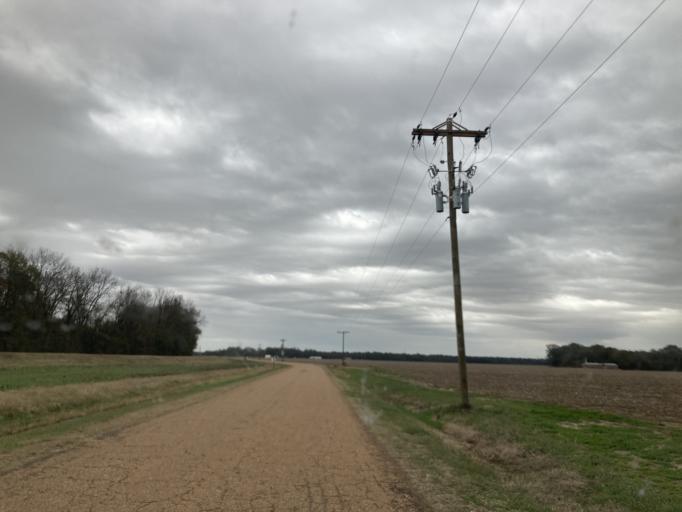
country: US
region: Mississippi
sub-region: Yazoo County
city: Yazoo City
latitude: 32.9801
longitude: -90.4206
